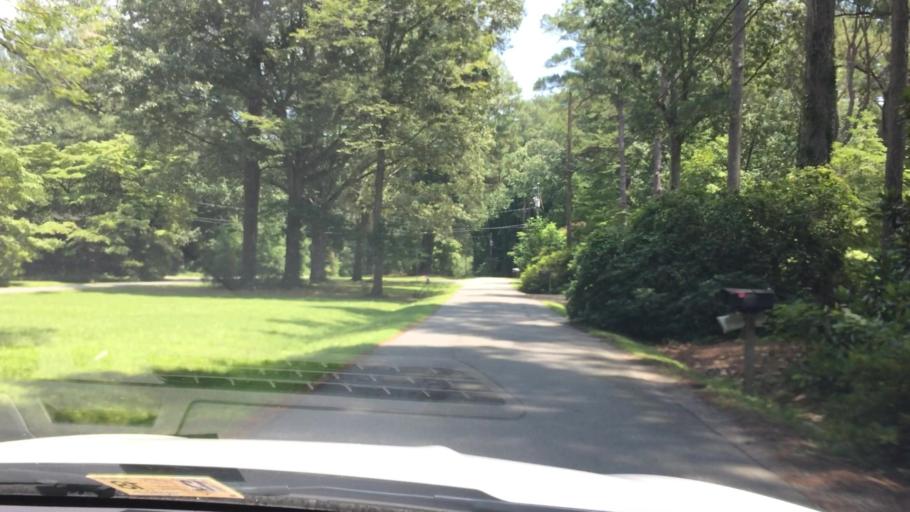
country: US
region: Virginia
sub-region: York County
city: Yorktown
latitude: 37.2102
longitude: -76.4768
